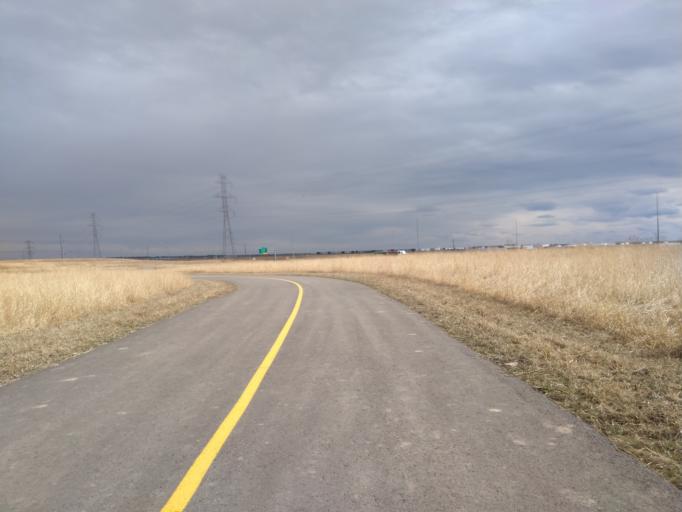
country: CA
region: Alberta
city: Airdrie
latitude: 51.1775
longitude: -114.0299
